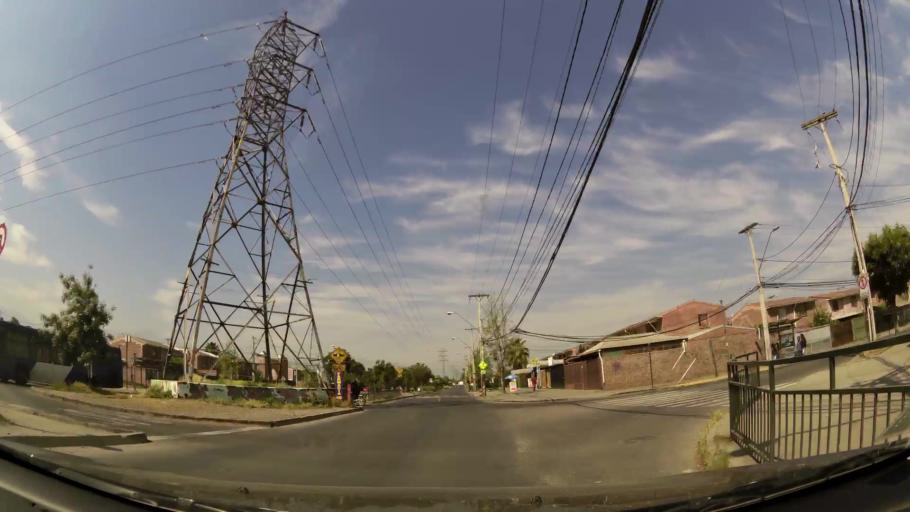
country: CL
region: Santiago Metropolitan
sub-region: Provincia de Santiago
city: La Pintana
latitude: -33.5756
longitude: -70.5989
